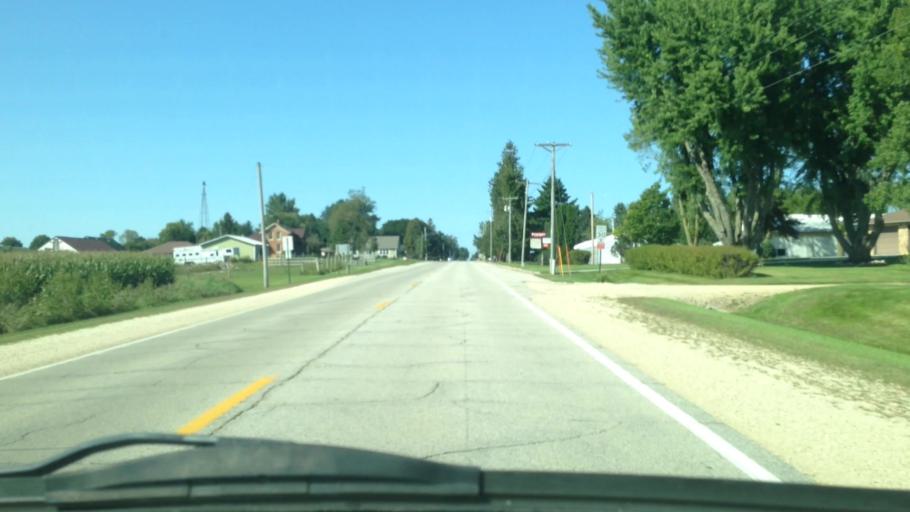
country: US
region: Minnesota
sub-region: Winona County
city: Lewiston
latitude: 43.9747
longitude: -91.8692
